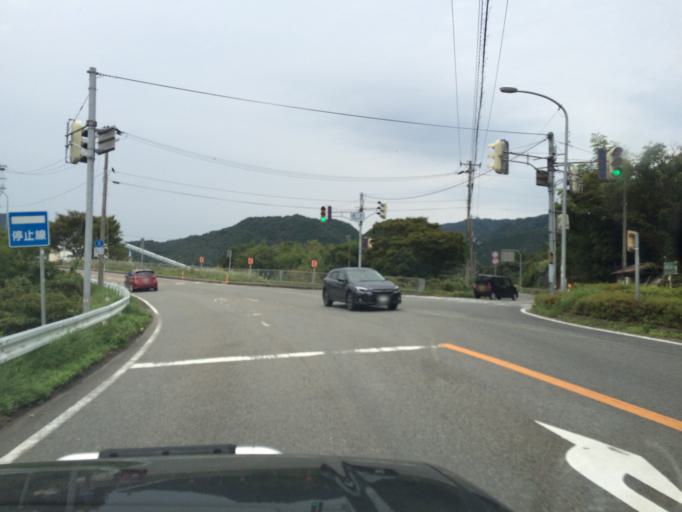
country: JP
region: Hyogo
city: Toyooka
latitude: 35.4169
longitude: 134.7914
